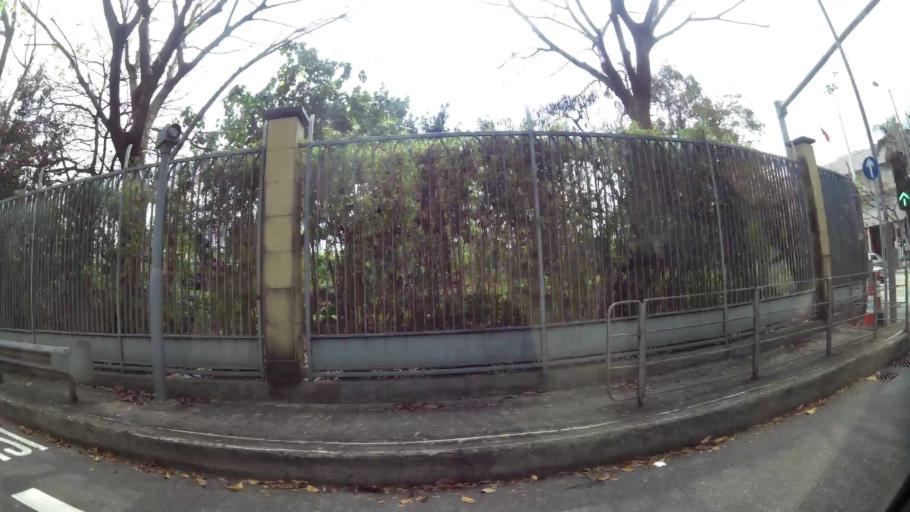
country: HK
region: Wanchai
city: Wan Chai
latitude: 22.2859
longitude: 114.1904
